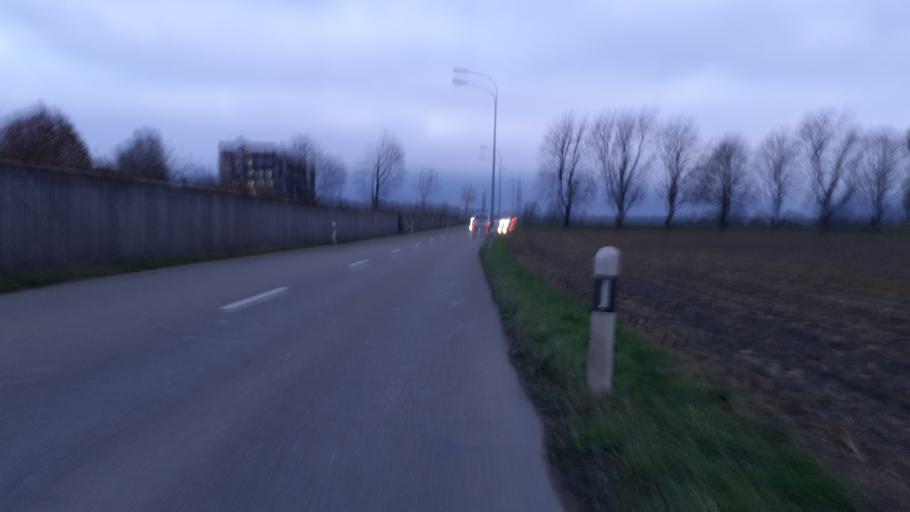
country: AT
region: Vorarlberg
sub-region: Politischer Bezirk Feldkirch
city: Mader
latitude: 47.3596
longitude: 9.6041
